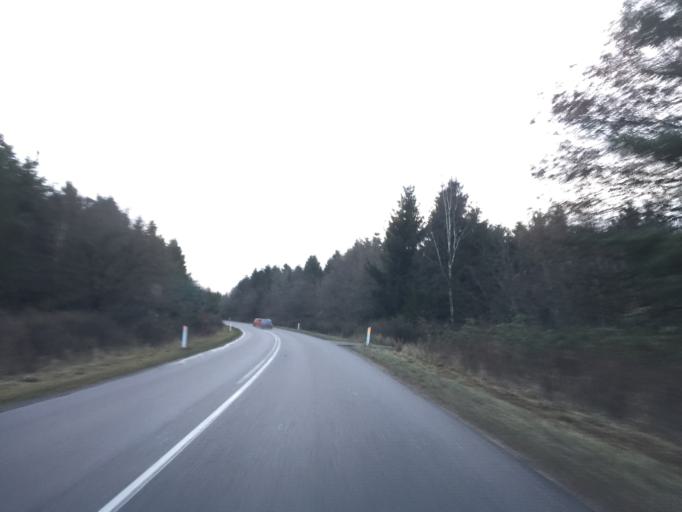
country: DK
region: Central Jutland
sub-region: Viborg Kommune
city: Bjerringbro
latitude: 56.3538
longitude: 9.6612
